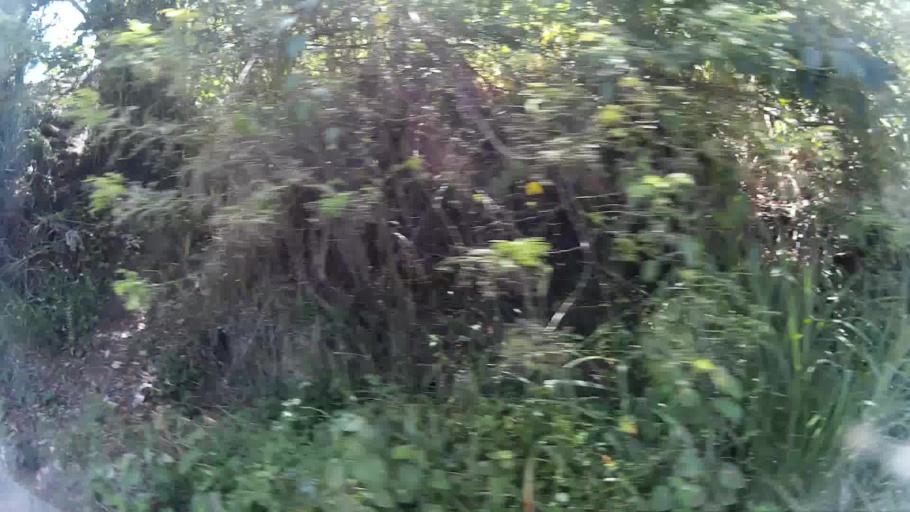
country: CO
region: Caldas
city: Belalcazar
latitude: 4.9428
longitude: -75.8383
